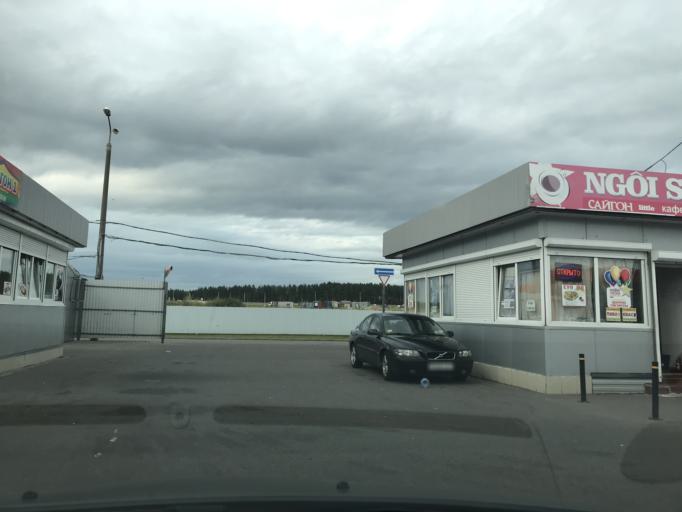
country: BY
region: Minsk
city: Borovlyany
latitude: 53.9649
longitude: 27.6261
